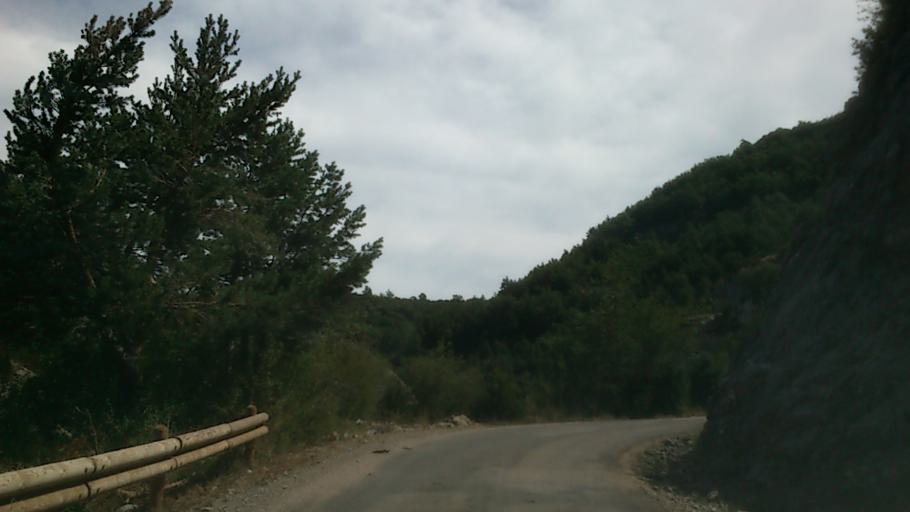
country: ES
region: Aragon
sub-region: Provincia de Huesca
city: Arguis
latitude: 42.3147
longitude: -0.2943
